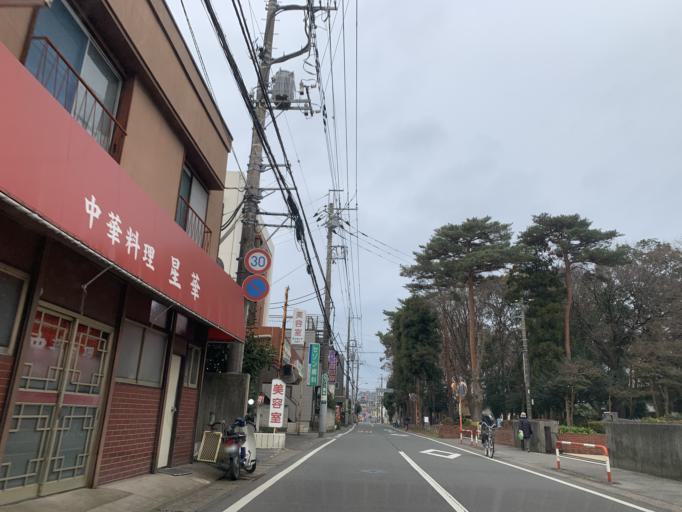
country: JP
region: Chiba
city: Nagareyama
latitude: 35.8809
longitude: 139.9181
